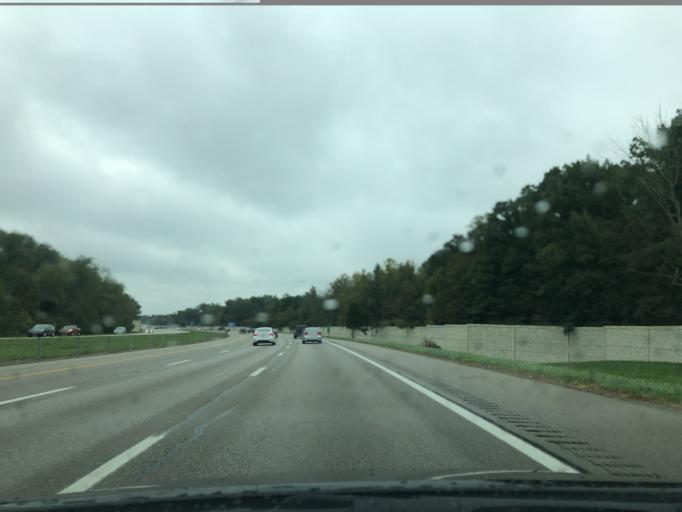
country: US
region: Ohio
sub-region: Hamilton County
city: Sixteen Mile Stand
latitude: 39.2537
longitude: -84.3278
